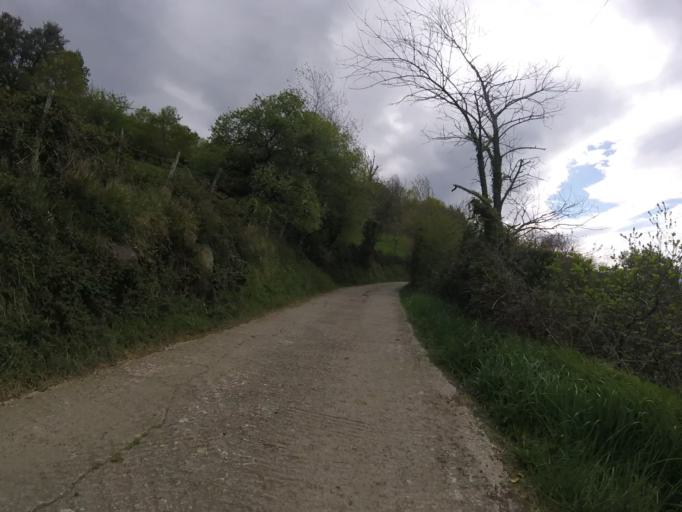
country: ES
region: Basque Country
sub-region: Provincia de Guipuzcoa
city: Aizarnazabal
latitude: 43.2525
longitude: -2.2078
